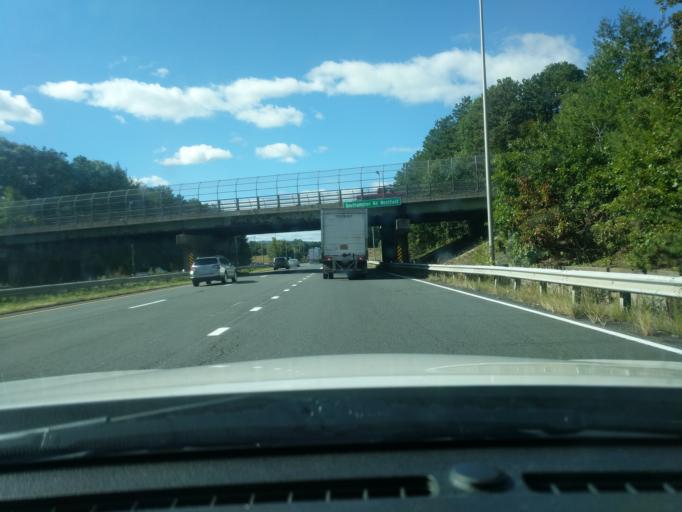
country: US
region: Massachusetts
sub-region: Hampden County
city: Westfield
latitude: 42.1444
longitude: -72.7308
